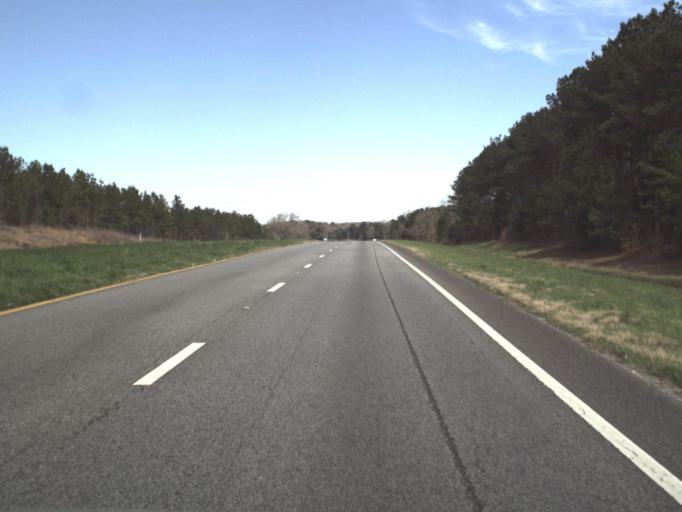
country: US
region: Florida
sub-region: Jackson County
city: Marianna
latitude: 30.8327
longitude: -85.3542
